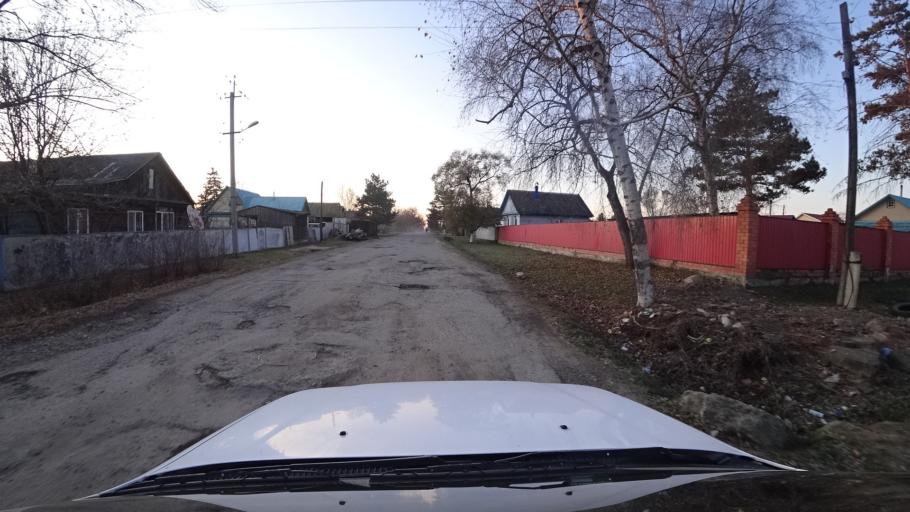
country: RU
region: Primorskiy
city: Dal'nerechensk
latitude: 45.9230
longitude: 133.7346
